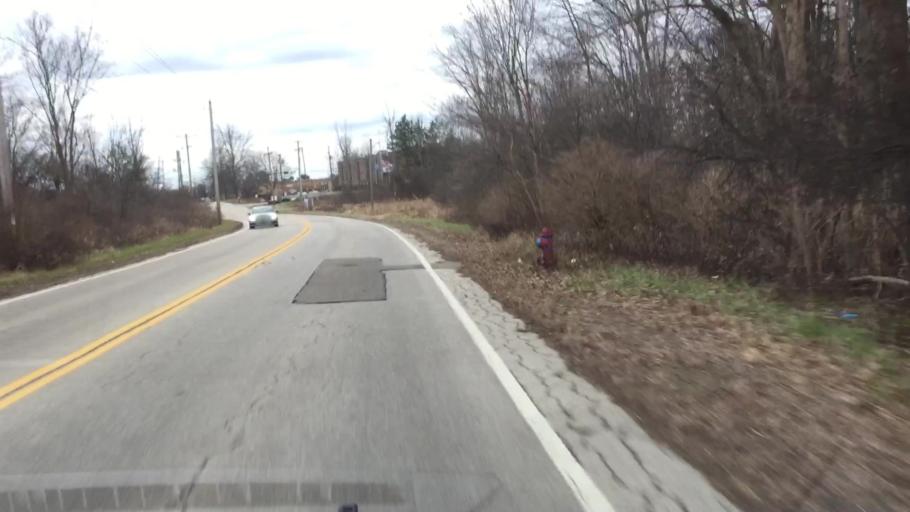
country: US
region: Ohio
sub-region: Summit County
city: Silver Lake
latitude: 41.1968
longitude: -81.4720
